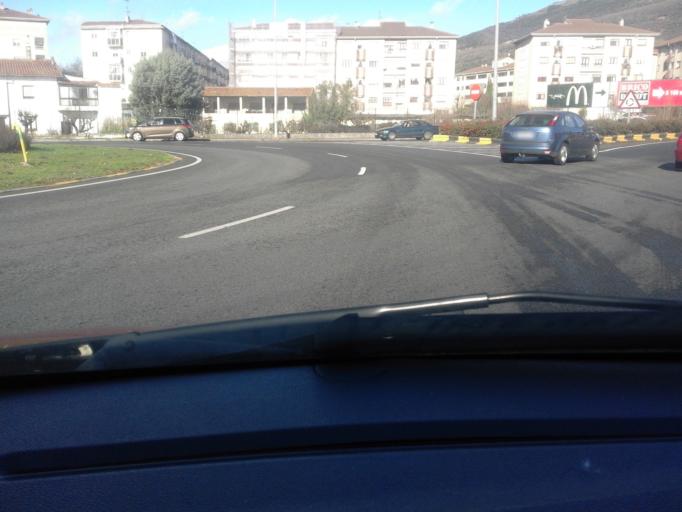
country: ES
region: Navarre
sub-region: Provincia de Navarra
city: Berriozar
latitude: 42.8322
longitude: -1.6670
